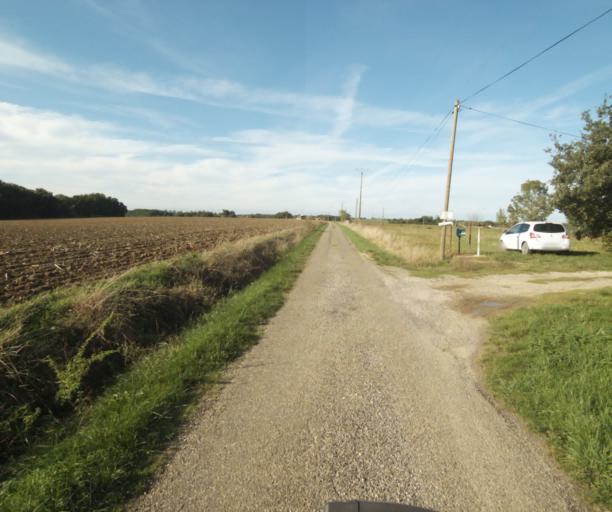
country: FR
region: Midi-Pyrenees
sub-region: Departement du Tarn-et-Garonne
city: Finhan
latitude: 43.9219
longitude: 1.1258
